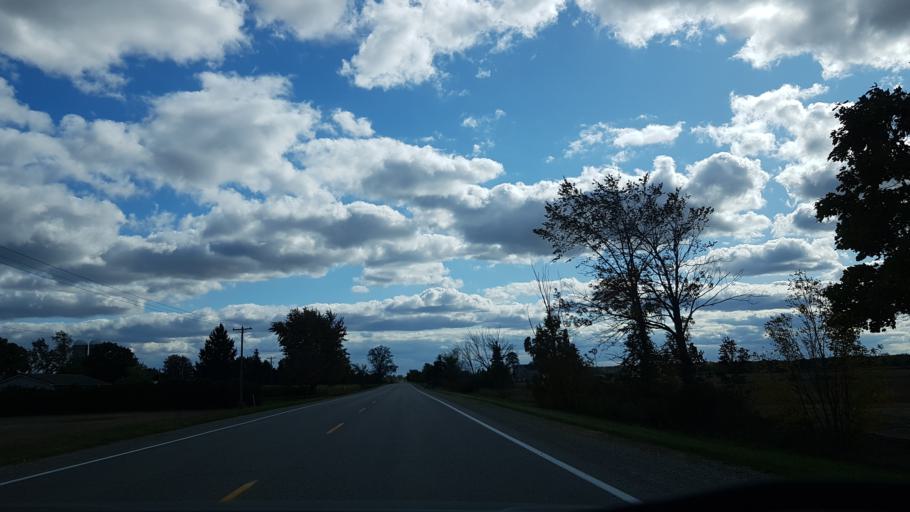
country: CA
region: Ontario
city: South Huron
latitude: 43.2363
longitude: -81.6894
